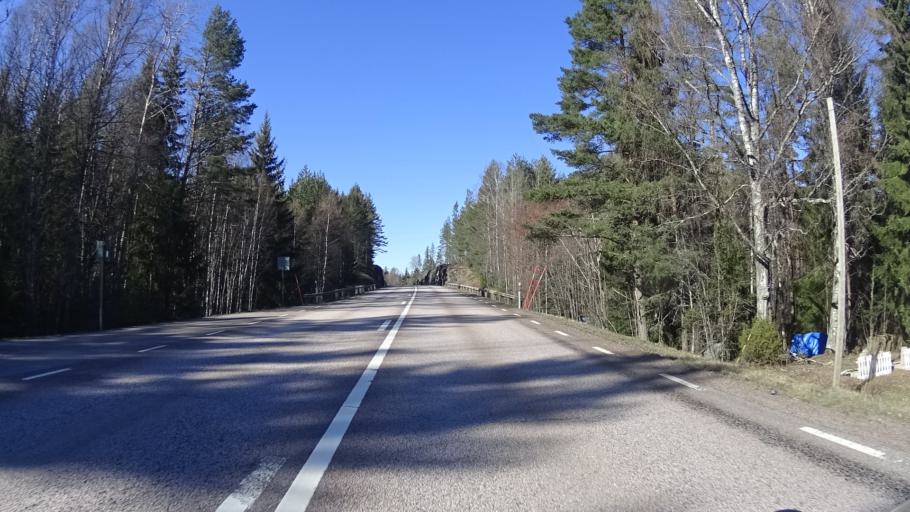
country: SE
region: Vaermland
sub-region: Karlstads Kommun
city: Edsvalla
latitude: 59.5926
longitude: 13.0091
